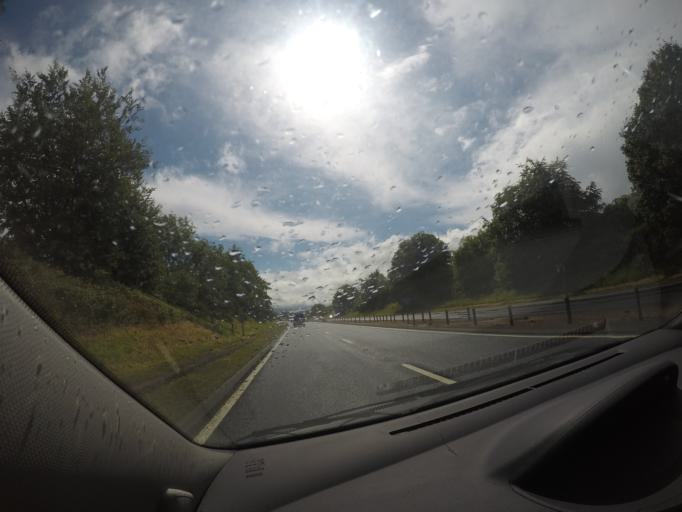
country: GB
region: Scotland
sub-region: Perth and Kinross
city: Auchterarder
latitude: 56.3174
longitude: -3.6535
